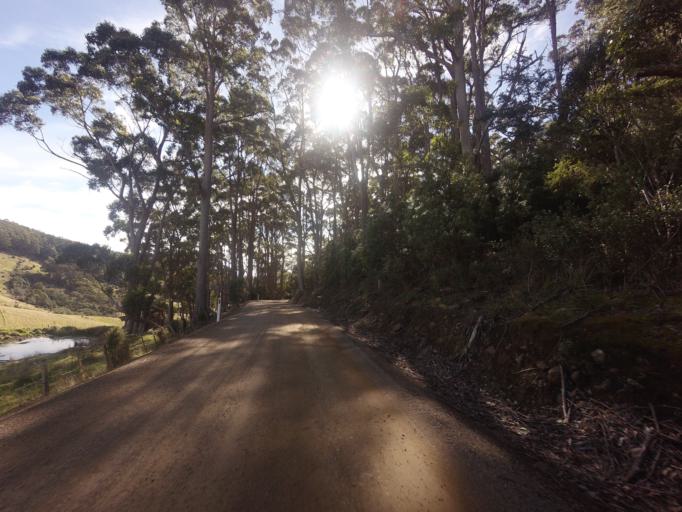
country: AU
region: Tasmania
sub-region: Clarence
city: Sandford
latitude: -43.1862
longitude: 147.7723
